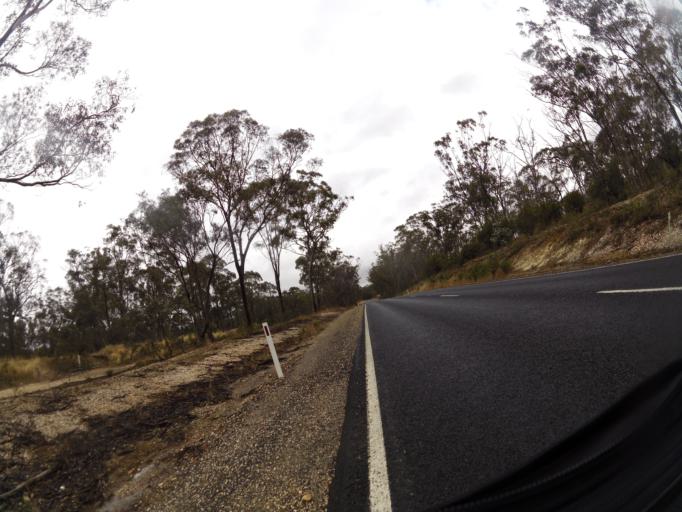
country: AU
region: Victoria
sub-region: Mount Alexander
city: Castlemaine
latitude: -37.0729
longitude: 144.1697
